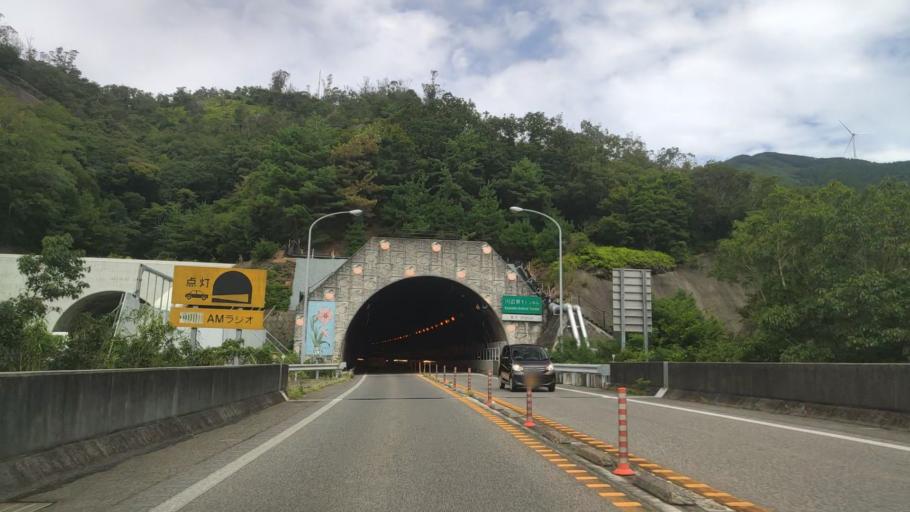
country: JP
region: Wakayama
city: Gobo
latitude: 33.9429
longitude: 135.1987
